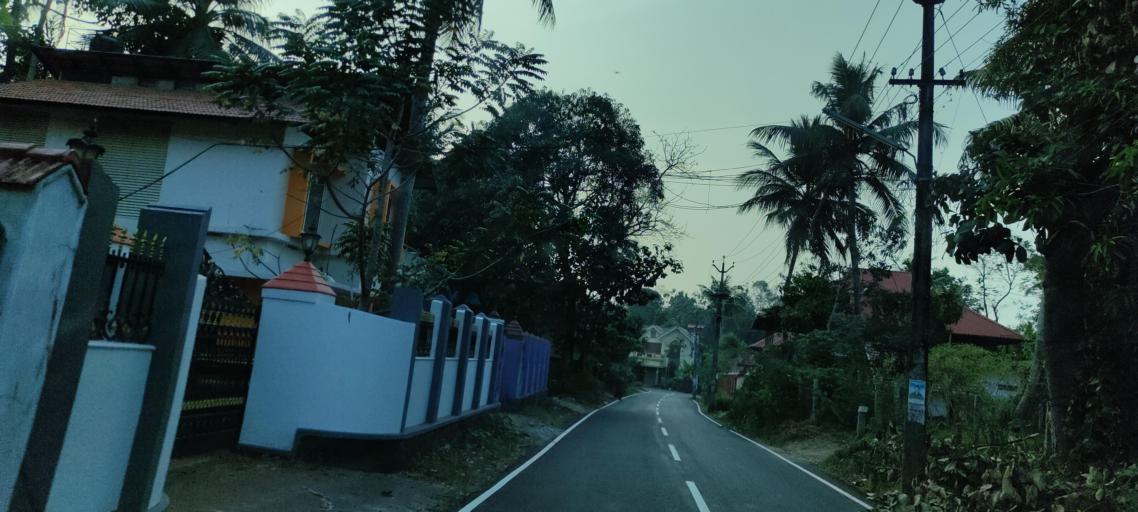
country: IN
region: Kerala
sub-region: Alappuzha
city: Mavelikara
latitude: 9.2773
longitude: 76.5529
